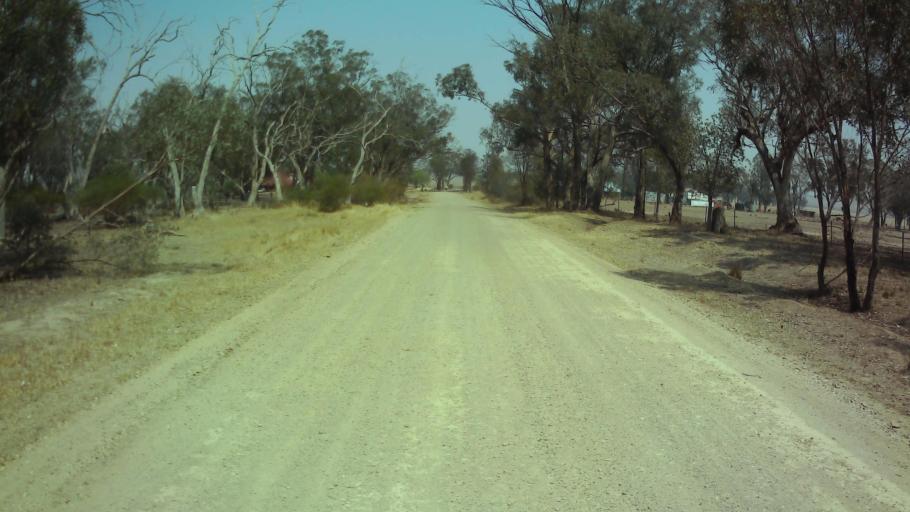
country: AU
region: New South Wales
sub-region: Weddin
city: Grenfell
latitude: -33.6447
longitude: 148.2606
